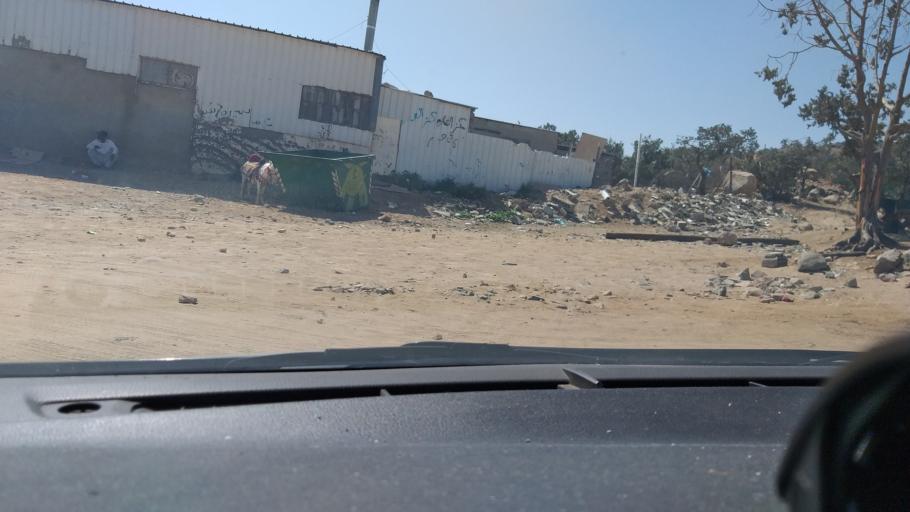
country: SA
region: Makkah
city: Ash Shafa
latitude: 21.0663
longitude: 40.3090
